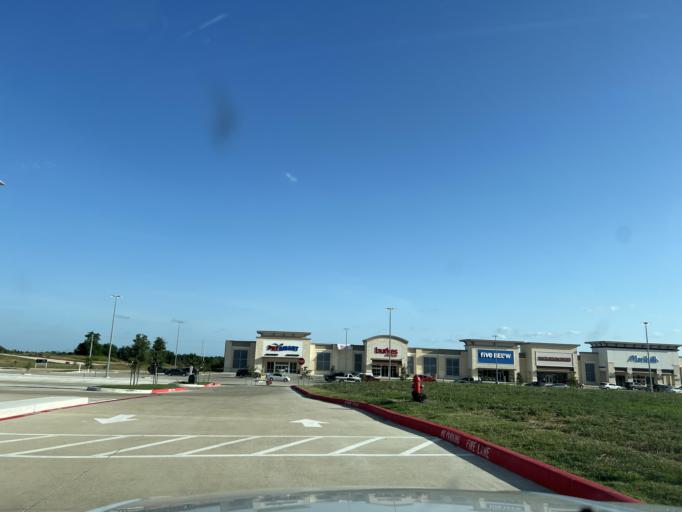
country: US
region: Texas
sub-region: Washington County
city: Brenham
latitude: 30.1417
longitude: -96.3822
